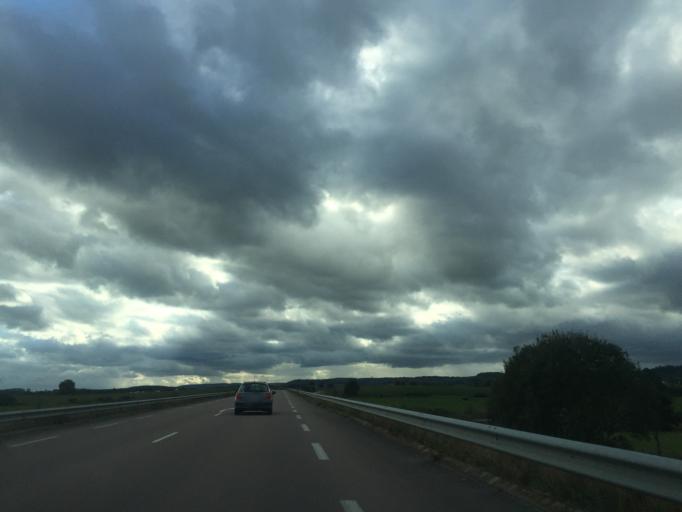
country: FR
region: Lorraine
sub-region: Departement des Vosges
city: Chatenois
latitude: 48.2973
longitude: 5.8707
